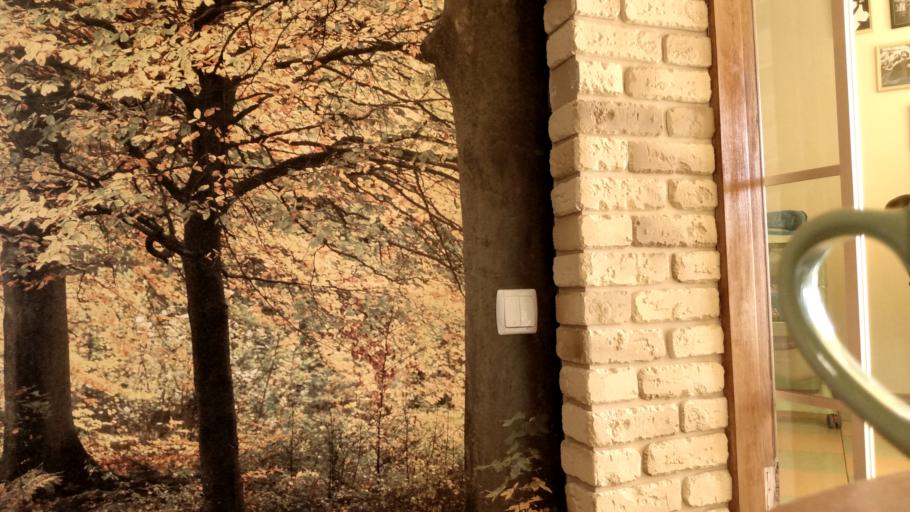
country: RU
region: Vologda
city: Imeni Zhelyabova
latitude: 58.8479
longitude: 36.8554
